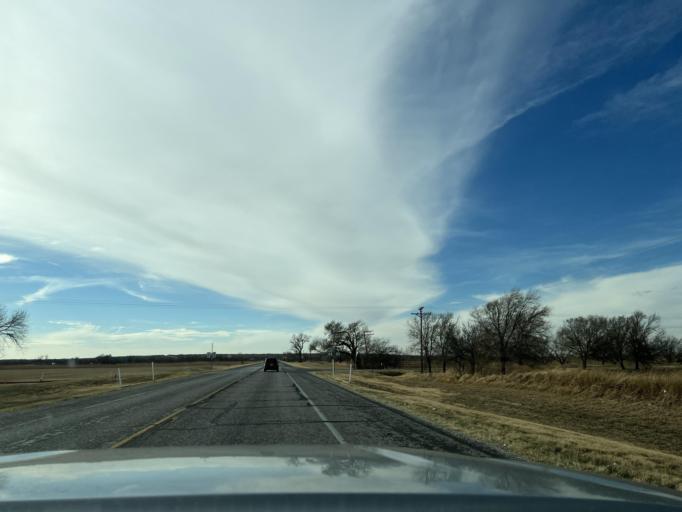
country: US
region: Texas
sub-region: Fisher County
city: Roby
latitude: 32.7612
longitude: -100.3007
